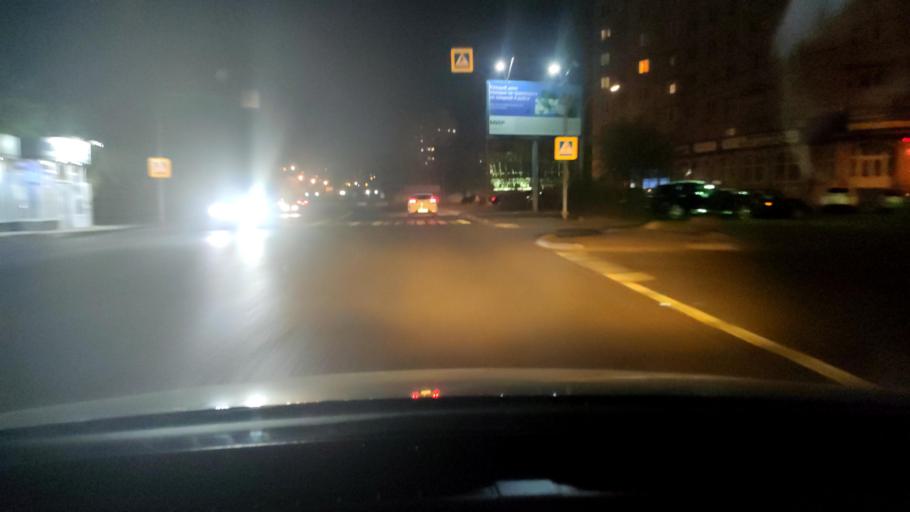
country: RU
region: Voronezj
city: Voronezh
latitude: 51.6836
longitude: 39.2042
